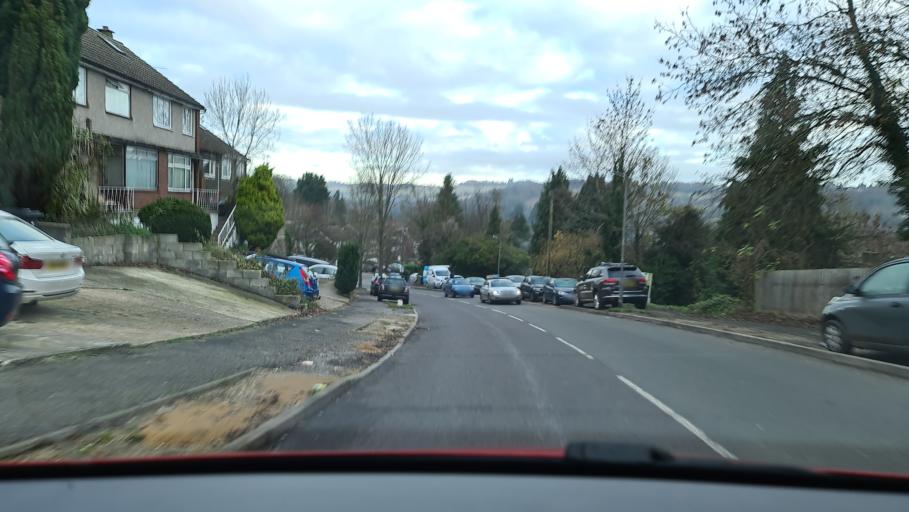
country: GB
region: England
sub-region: Buckinghamshire
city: High Wycombe
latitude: 51.6372
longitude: -0.7568
